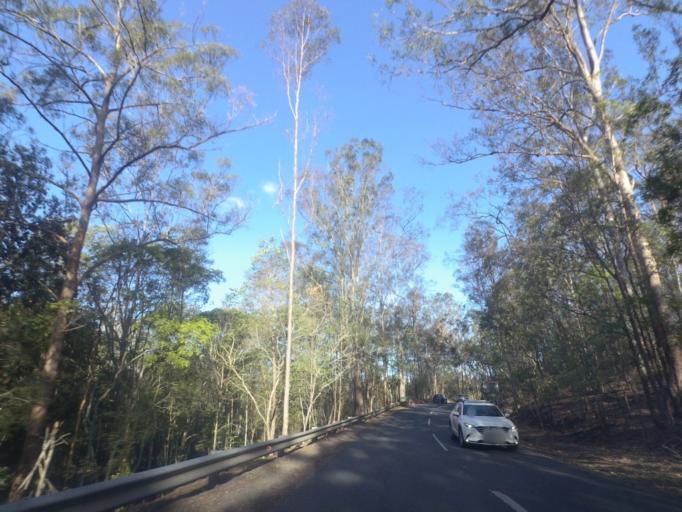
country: AU
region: Queensland
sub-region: Brisbane
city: Taringa
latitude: -27.4654
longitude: 152.9664
